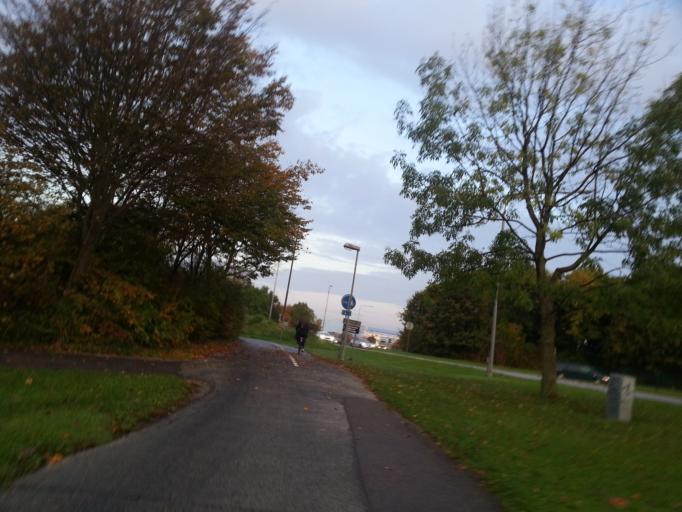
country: SE
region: Skane
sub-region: Lunds Kommun
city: Lund
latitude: 55.7140
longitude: 13.1644
